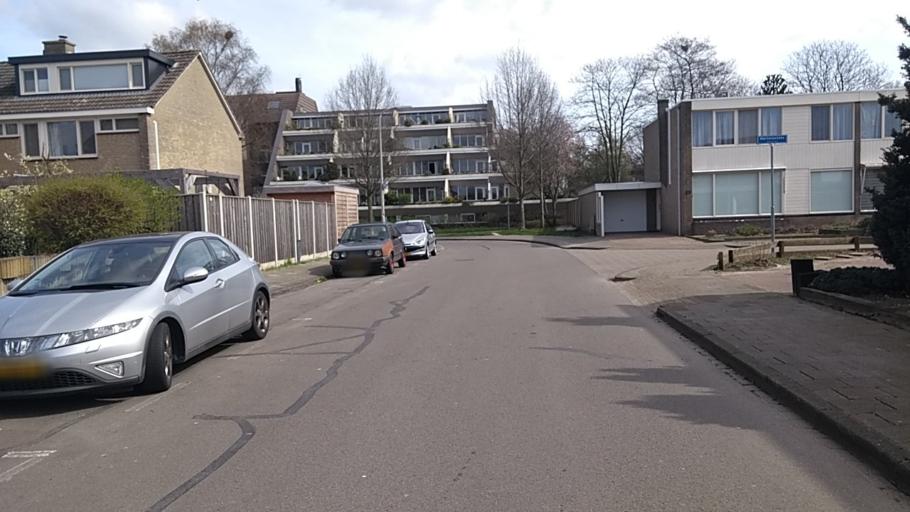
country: NL
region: Overijssel
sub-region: Gemeente Almelo
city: Almelo
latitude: 52.3803
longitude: 6.6751
